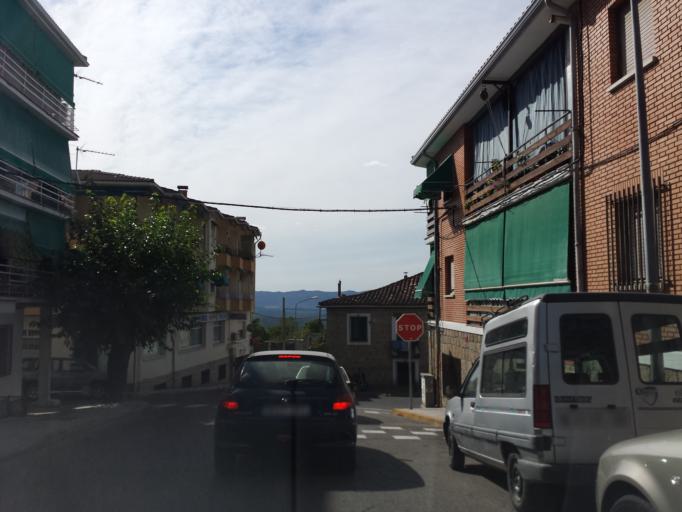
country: ES
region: Castille and Leon
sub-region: Provincia de Avila
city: Piedralaves
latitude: 40.3199
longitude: -4.6975
